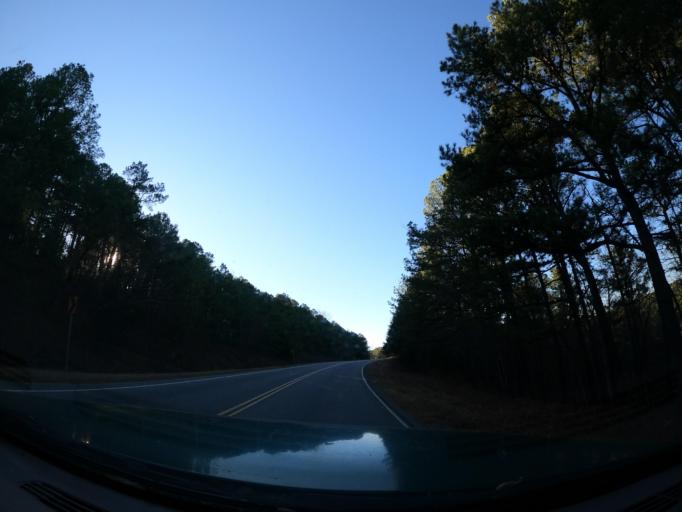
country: US
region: Oklahoma
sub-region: Latimer County
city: Wilburton
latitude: 35.0009
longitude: -95.3369
